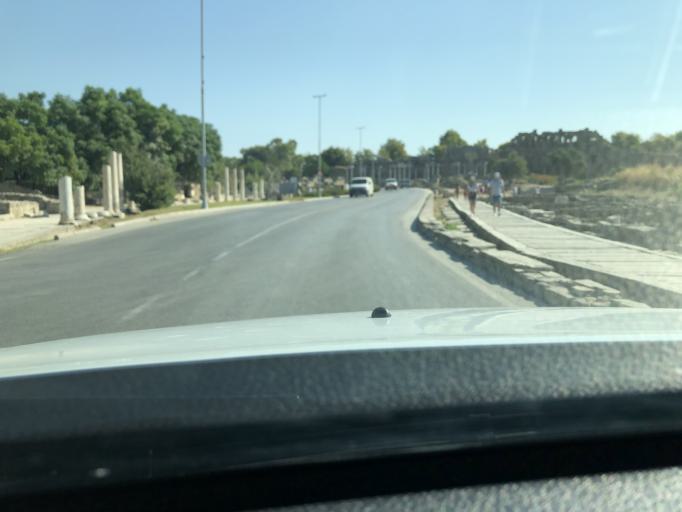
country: TR
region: Antalya
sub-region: Manavgat
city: Side
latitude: 36.7703
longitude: 31.3933
